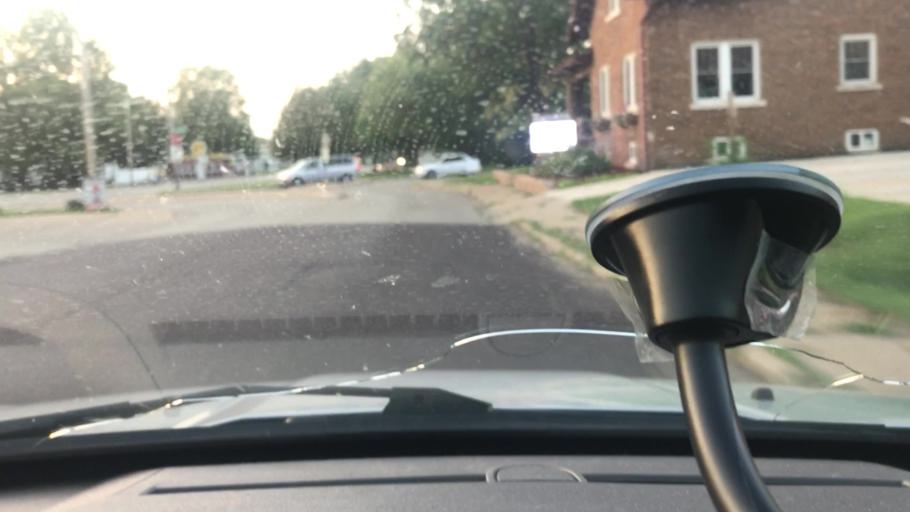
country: US
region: Illinois
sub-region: Tazewell County
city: Pekin
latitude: 40.5745
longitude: -89.6409
